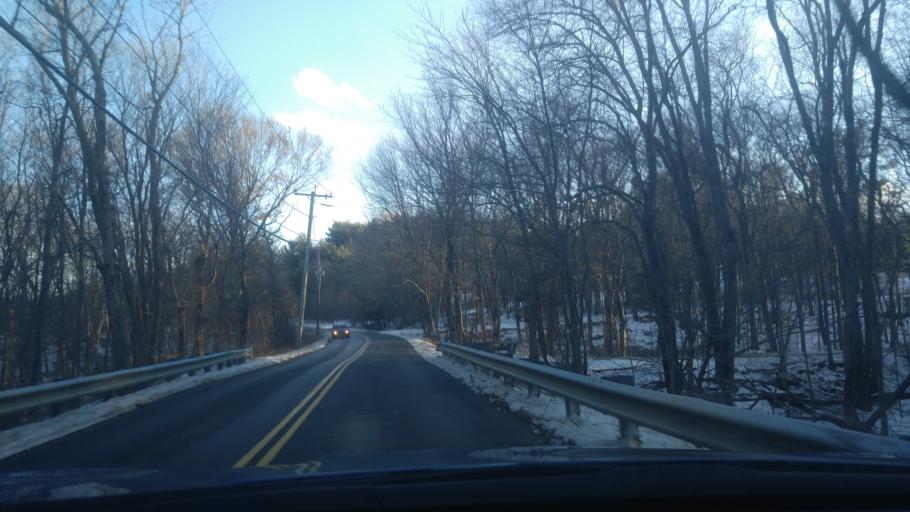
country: US
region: Rhode Island
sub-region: Kent County
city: Coventry
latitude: 41.7146
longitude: -71.6523
